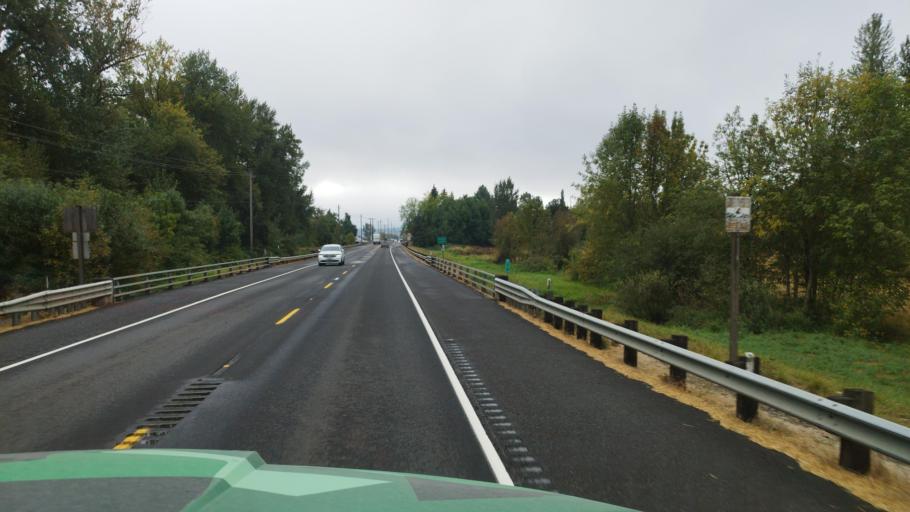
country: US
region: Oregon
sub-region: Washington County
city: Forest Grove
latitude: 45.4413
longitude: -123.1409
